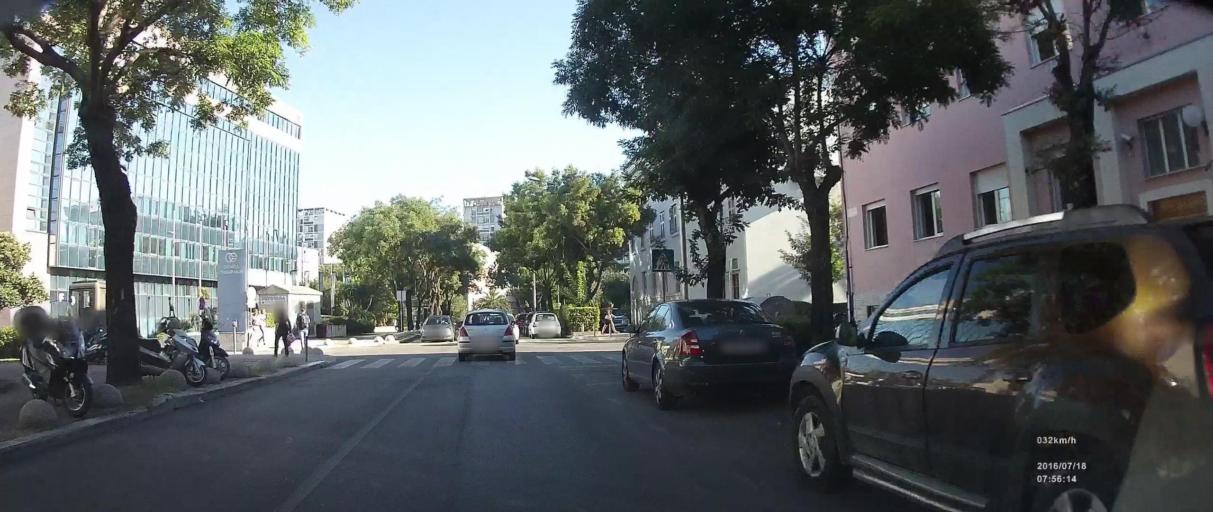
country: HR
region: Splitsko-Dalmatinska
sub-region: Grad Split
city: Split
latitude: 43.5155
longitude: 16.4422
